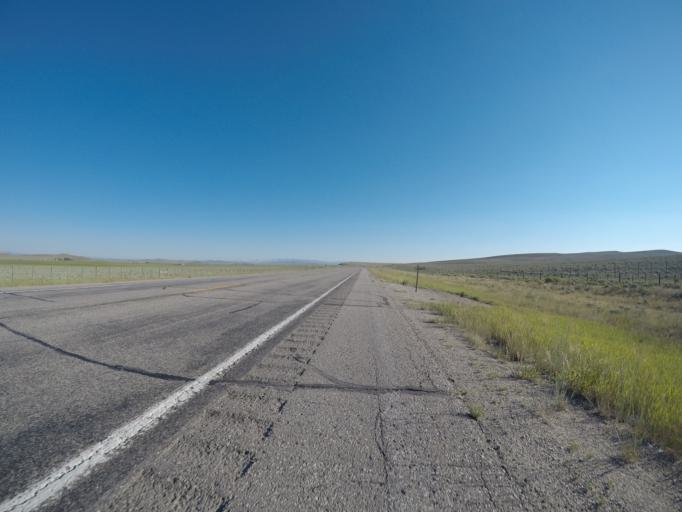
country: US
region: Wyoming
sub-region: Sublette County
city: Pinedale
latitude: 42.9276
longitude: -110.0809
